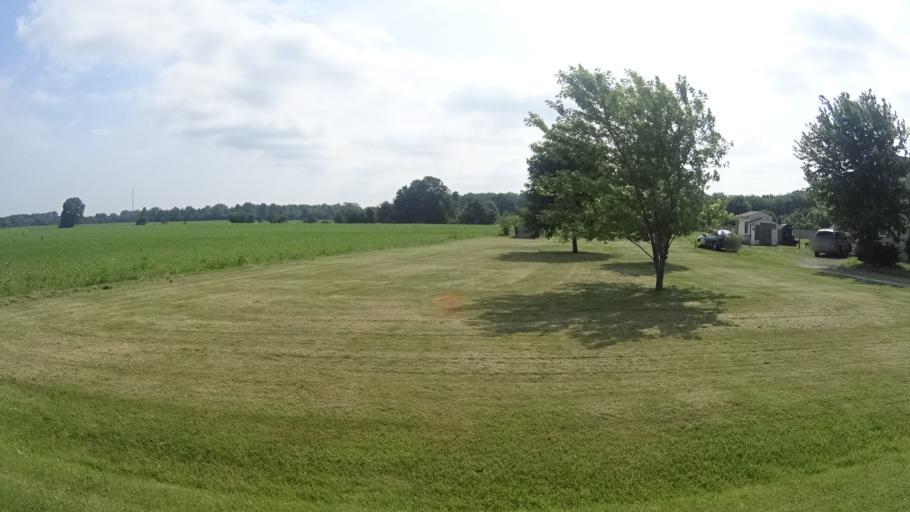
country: US
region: Ohio
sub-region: Lorain County
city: Vermilion
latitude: 41.3769
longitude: -82.4401
